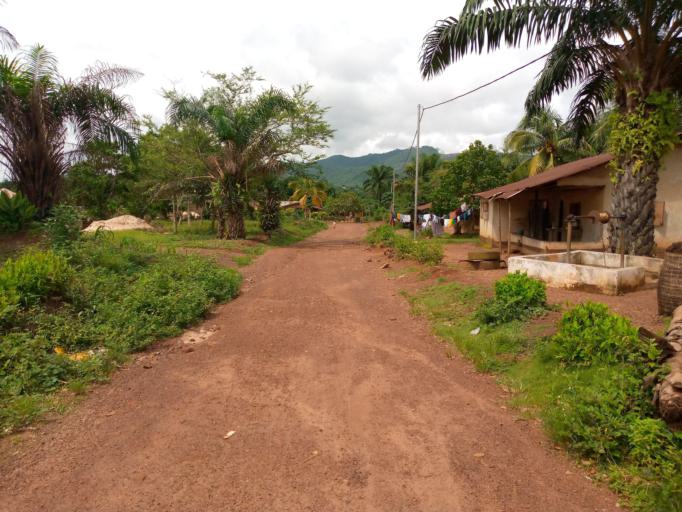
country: SL
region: Southern Province
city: Mogbwemo
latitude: 7.7598
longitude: -12.3083
